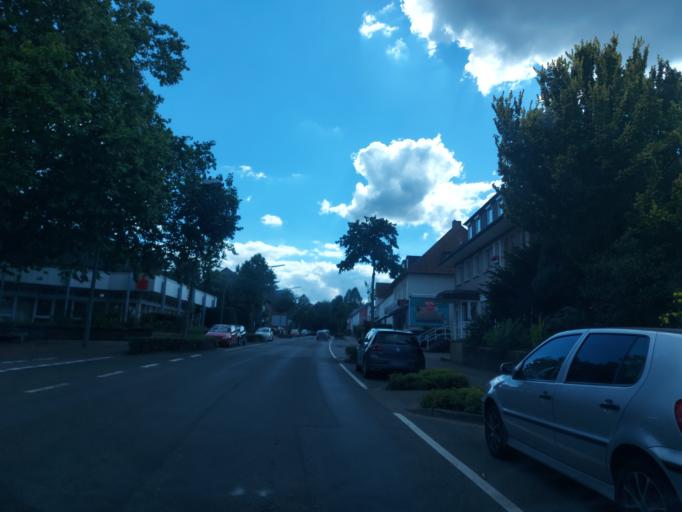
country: DE
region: Lower Saxony
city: Hagen
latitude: 52.2233
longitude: 8.0085
